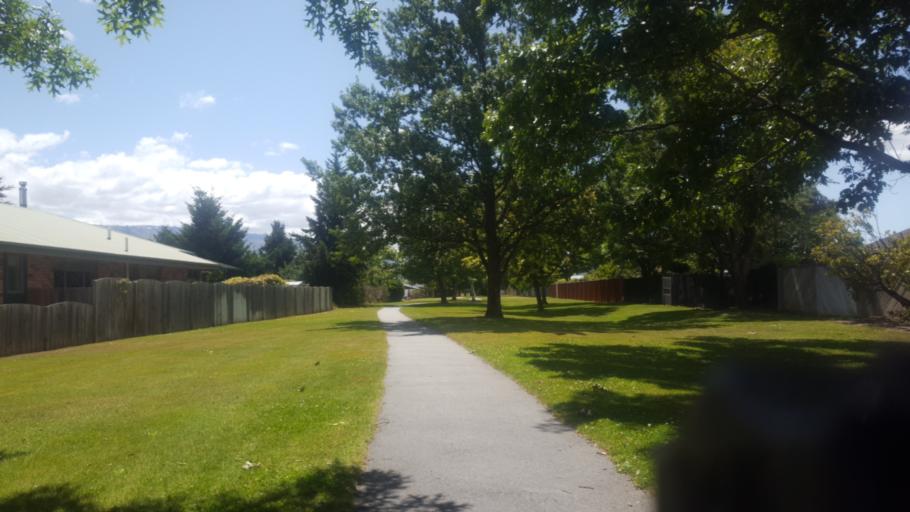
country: NZ
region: Otago
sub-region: Queenstown-Lakes District
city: Wanaka
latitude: -45.0424
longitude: 169.1993
